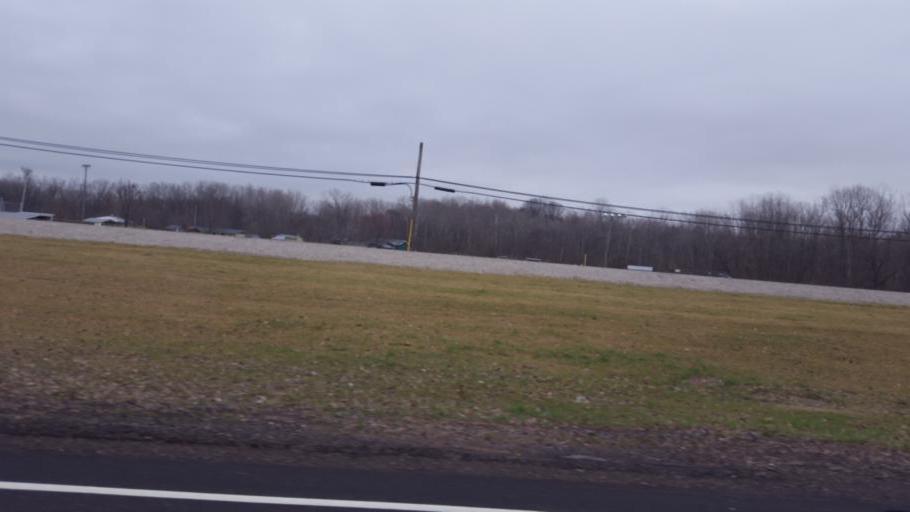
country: US
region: Ohio
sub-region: Knox County
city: Fredericktown
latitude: 40.4869
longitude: -82.5450
